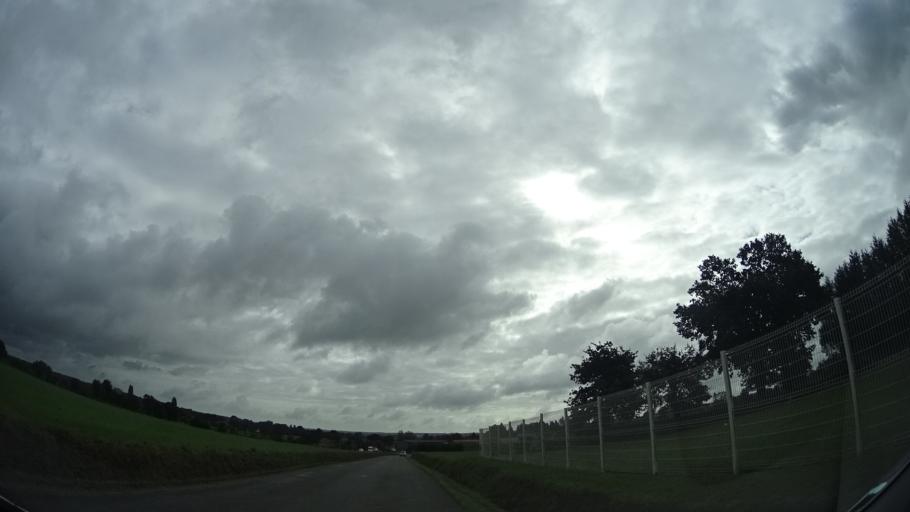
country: FR
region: Brittany
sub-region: Departement d'Ille-et-Vilaine
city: Montreuil-sur-Ille
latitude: 48.2978
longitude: -1.6454
